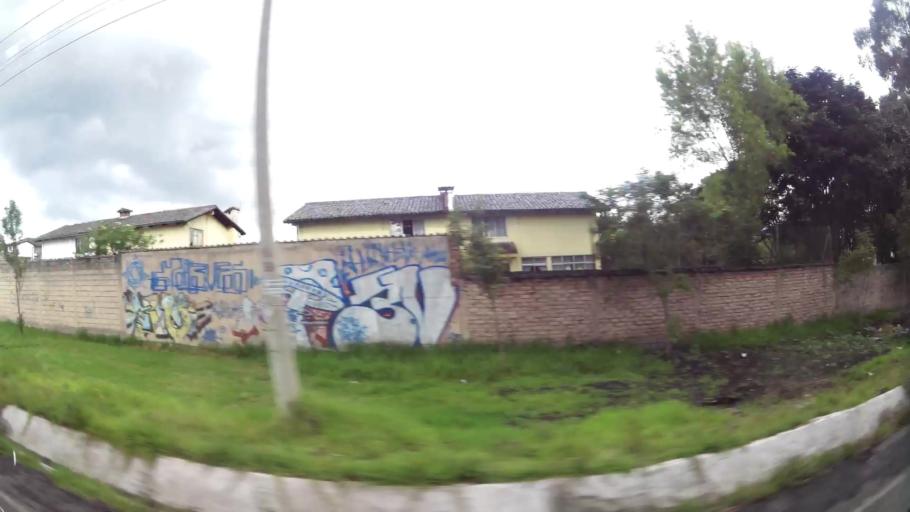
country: EC
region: Pichincha
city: Sangolqui
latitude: -0.3420
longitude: -78.4504
